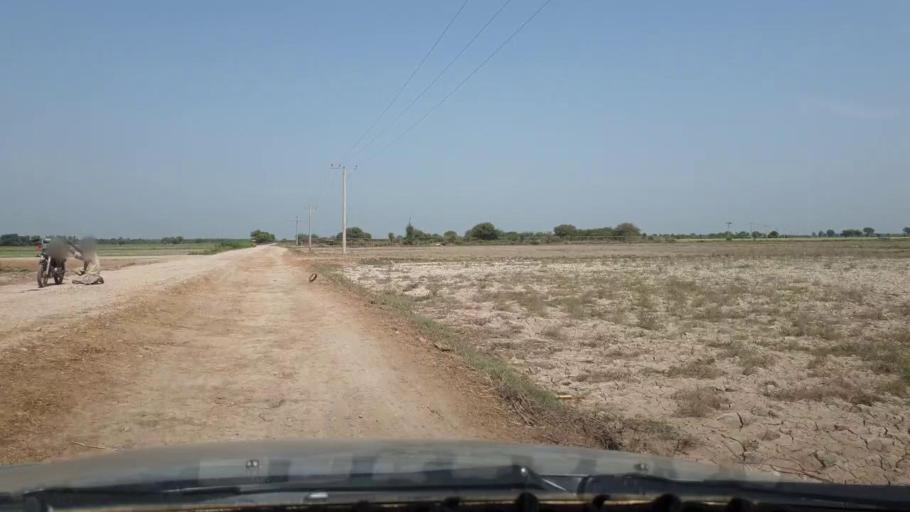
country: PK
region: Sindh
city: Tando Muhammad Khan
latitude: 25.1558
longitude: 68.6338
